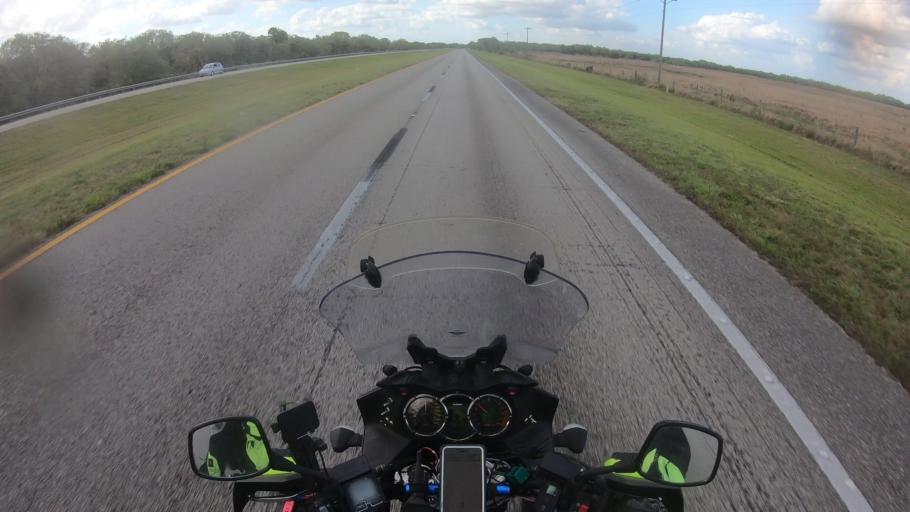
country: US
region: Florida
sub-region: Glades County
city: Moore Haven
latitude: 26.8866
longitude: -81.2332
